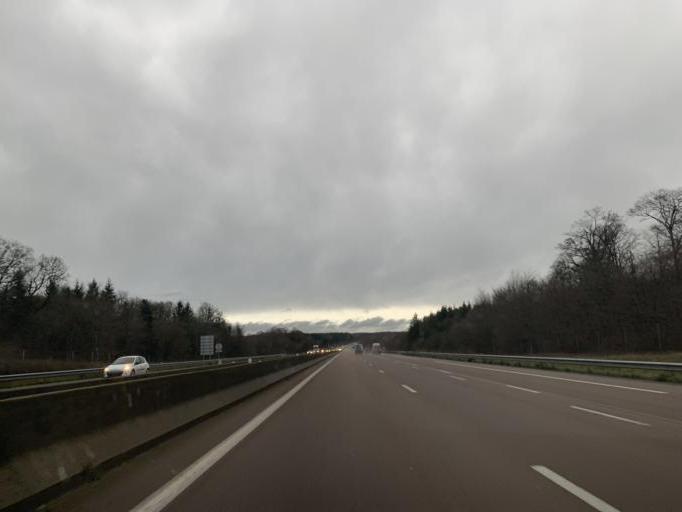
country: FR
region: Bourgogne
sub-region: Departement de la Cote-d'Or
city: Selongey
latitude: 47.6476
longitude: 5.1786
